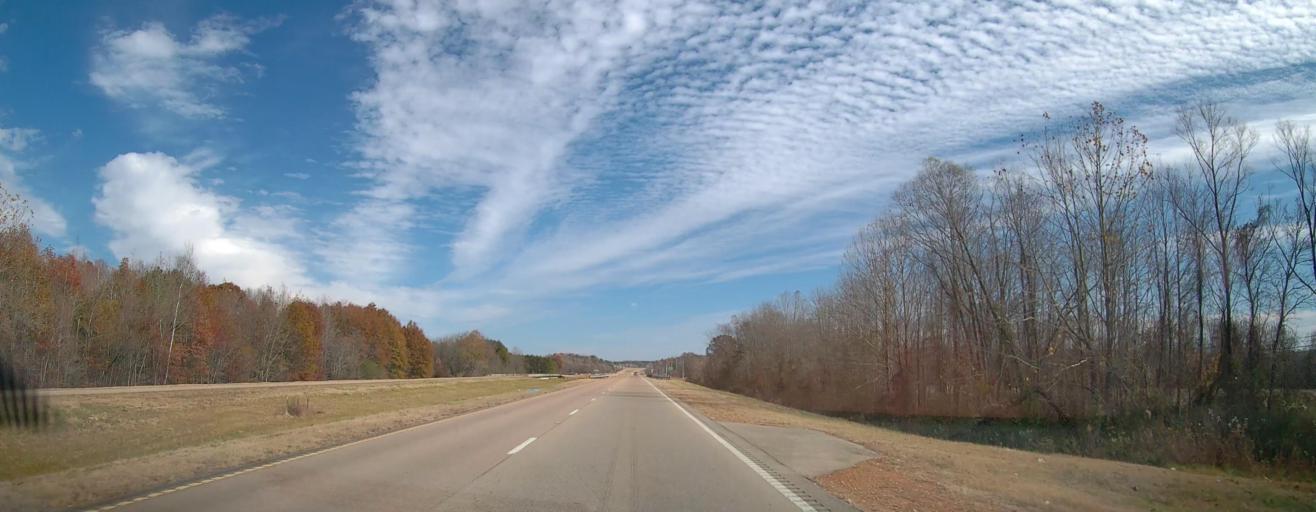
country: US
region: Mississippi
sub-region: Tippah County
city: Ripley
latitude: 34.9527
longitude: -88.8796
